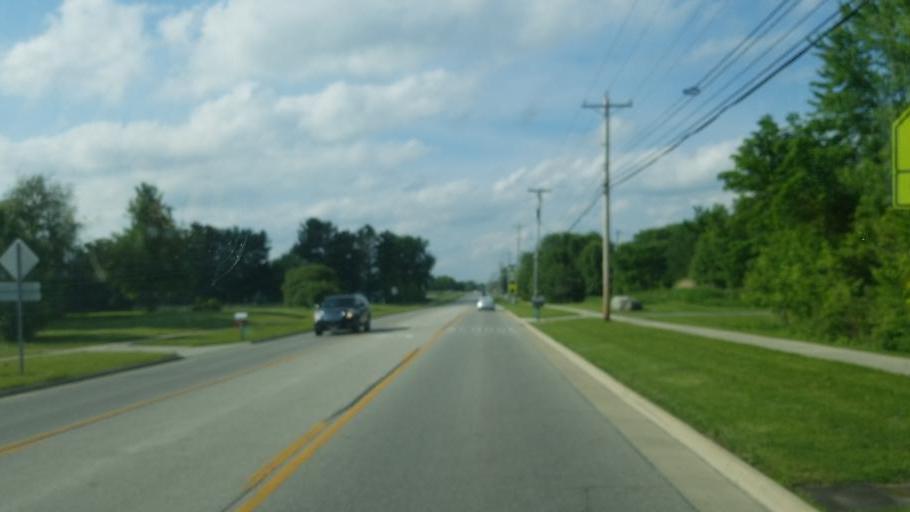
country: US
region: Ohio
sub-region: Franklin County
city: Westerville
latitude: 40.1524
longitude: -82.9009
